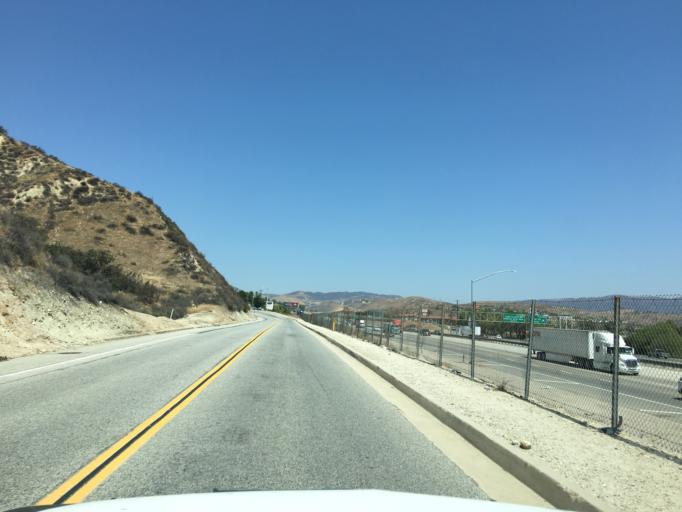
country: US
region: California
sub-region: Los Angeles County
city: Castaic
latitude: 34.4858
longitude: -118.6169
